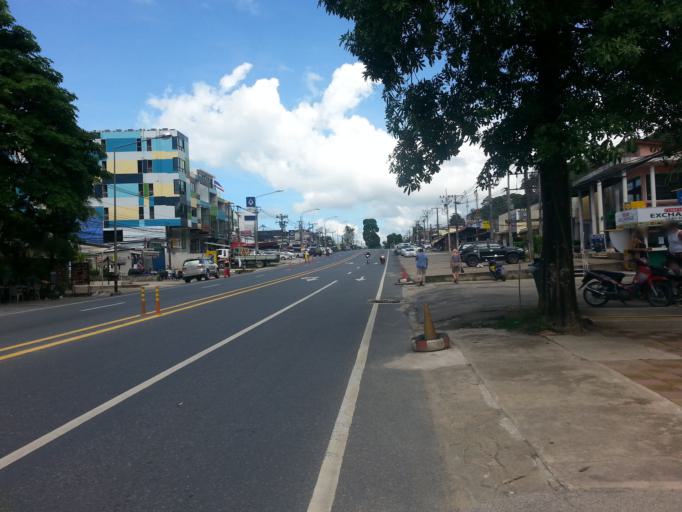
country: TH
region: Phangnga
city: Ban Khao Lak
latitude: 8.6452
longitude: 98.2517
